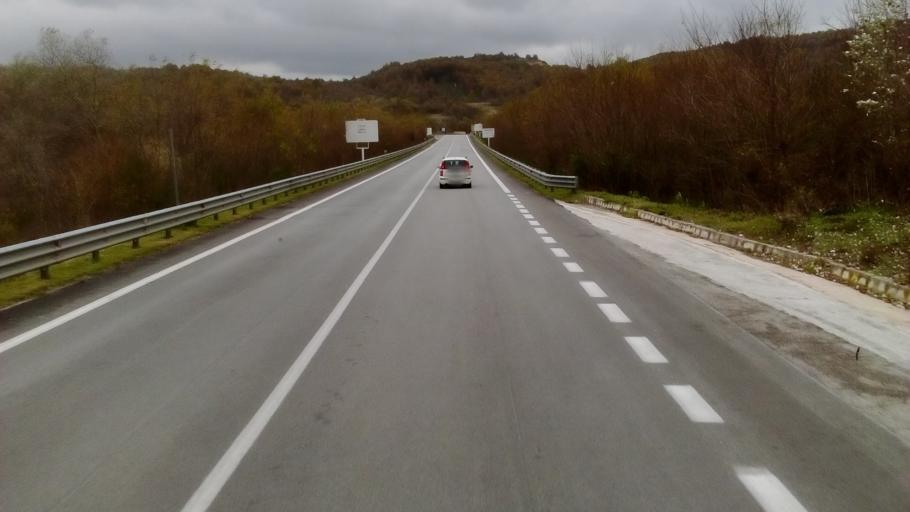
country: IT
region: Molise
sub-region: Provincia di Isernia
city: Sessano del Molise
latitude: 41.6251
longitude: 14.3136
